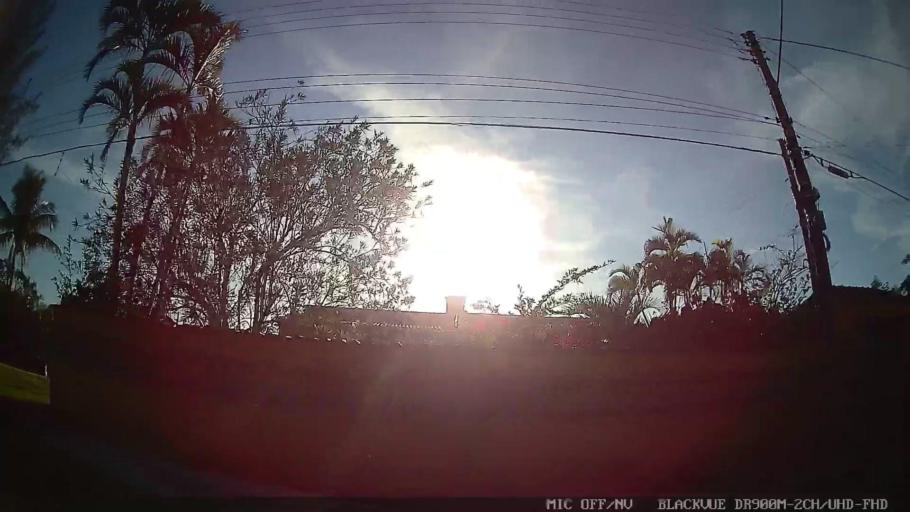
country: BR
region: Sao Paulo
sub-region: Iguape
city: Iguape
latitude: -24.7561
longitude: -47.5689
